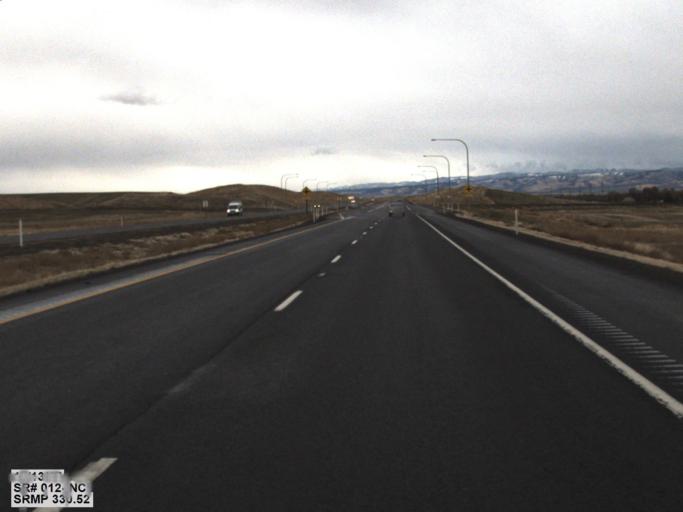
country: US
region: Washington
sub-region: Walla Walla County
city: Garrett
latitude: 46.0546
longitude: -118.4614
